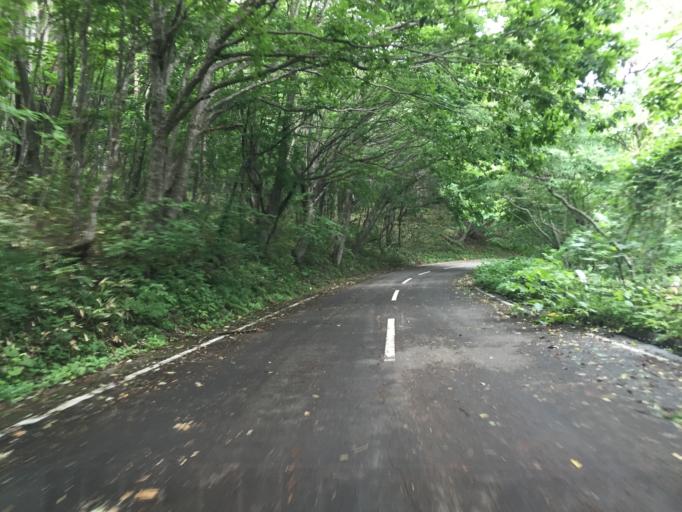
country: JP
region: Fukushima
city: Nihommatsu
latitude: 37.6623
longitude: 140.3236
